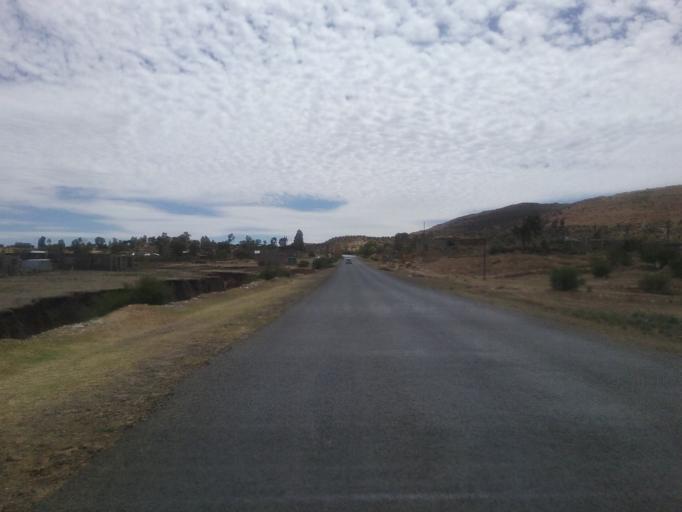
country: LS
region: Mafeteng
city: Mafeteng
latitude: -29.8441
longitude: 27.2300
